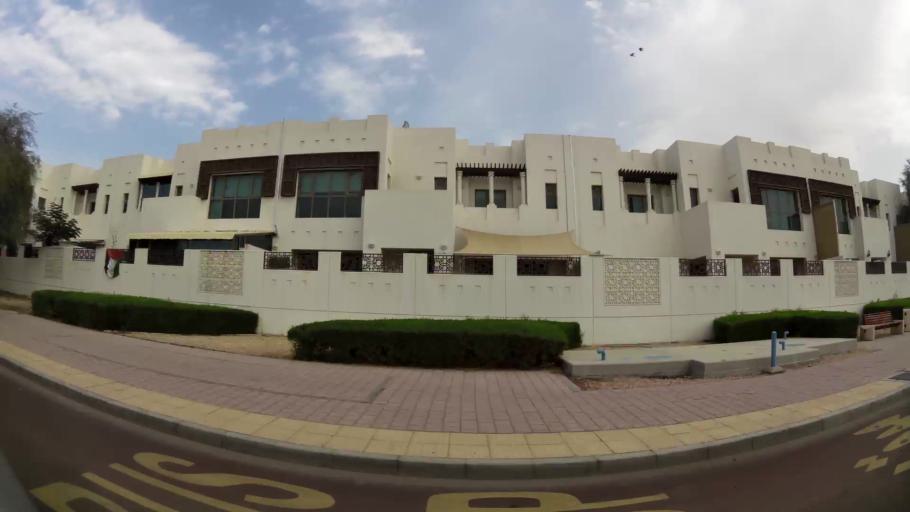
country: AE
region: Abu Dhabi
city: Abu Dhabi
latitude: 24.4545
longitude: 54.3518
